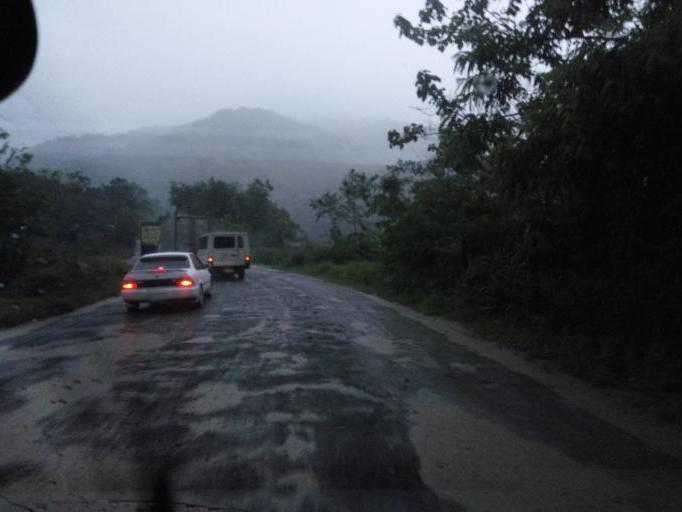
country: PH
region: Cagayan Valley
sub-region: Province of Nueva Vizcaya
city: Santa Fe
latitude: 16.1956
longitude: 120.9481
